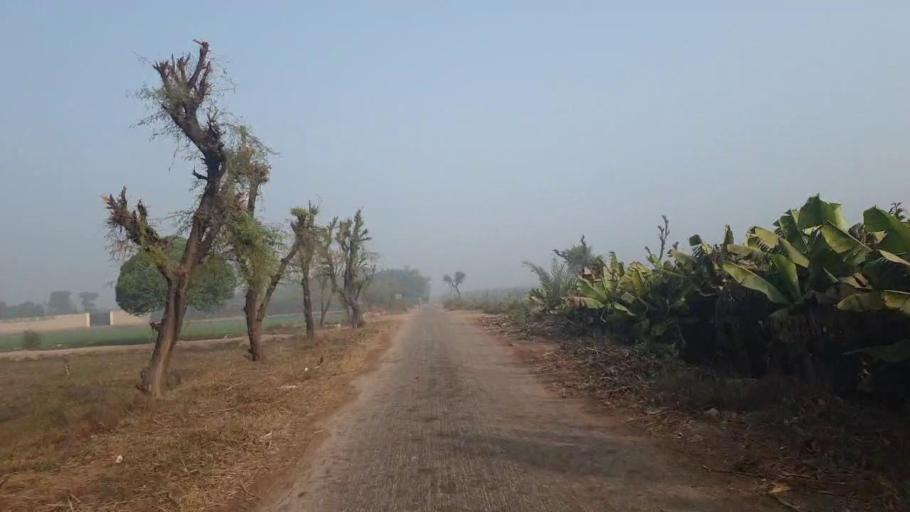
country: PK
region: Sindh
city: Tando Adam
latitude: 25.7877
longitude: 68.6334
